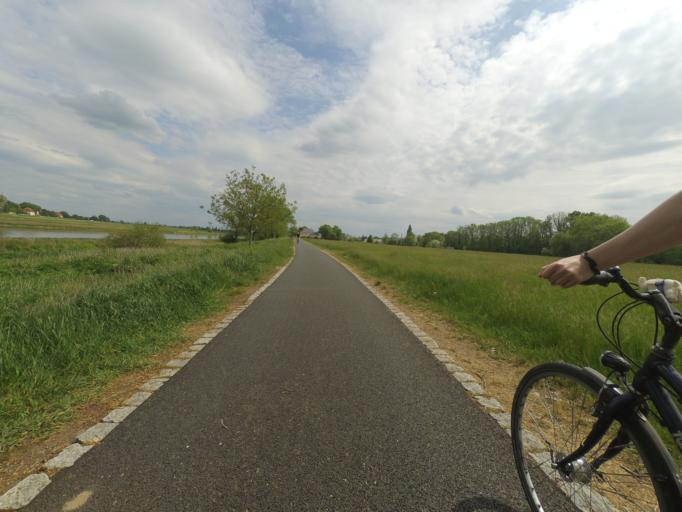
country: DE
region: Saxony
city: Strehla
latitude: 51.3558
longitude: 13.2322
